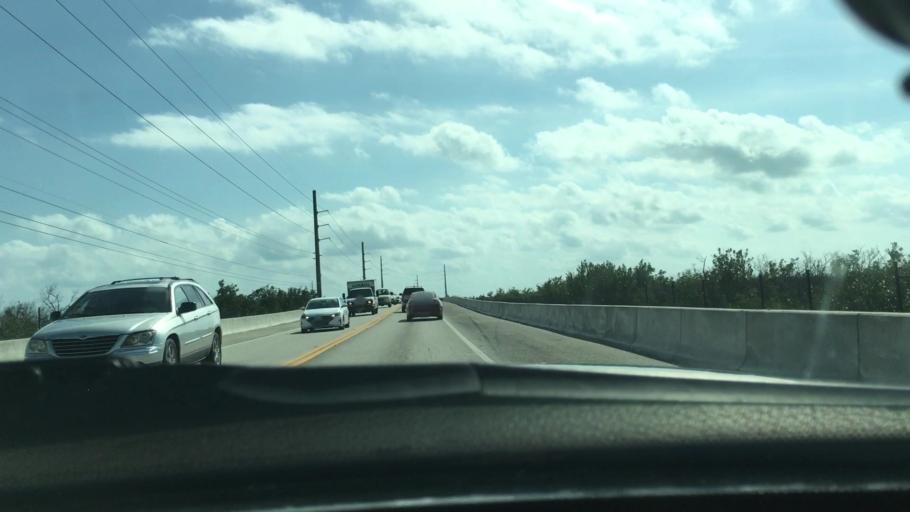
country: US
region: Florida
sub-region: Monroe County
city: Big Pine Key
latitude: 24.6548
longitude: -81.3357
